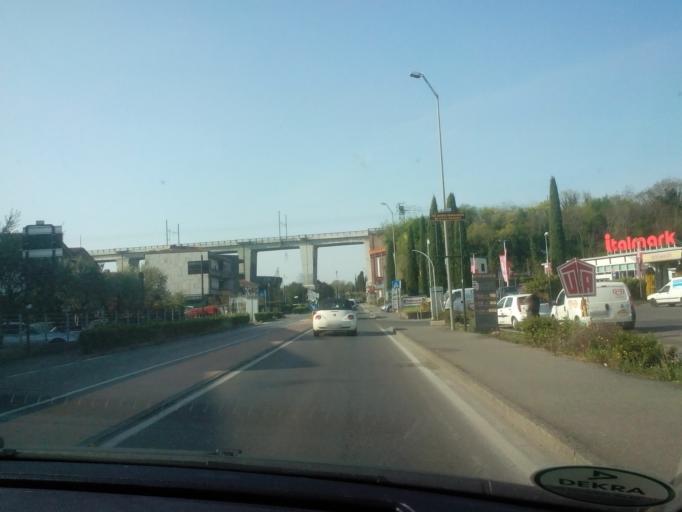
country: IT
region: Lombardy
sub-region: Provincia di Brescia
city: Desenzano del Garda
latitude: 45.4683
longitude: 10.5283
